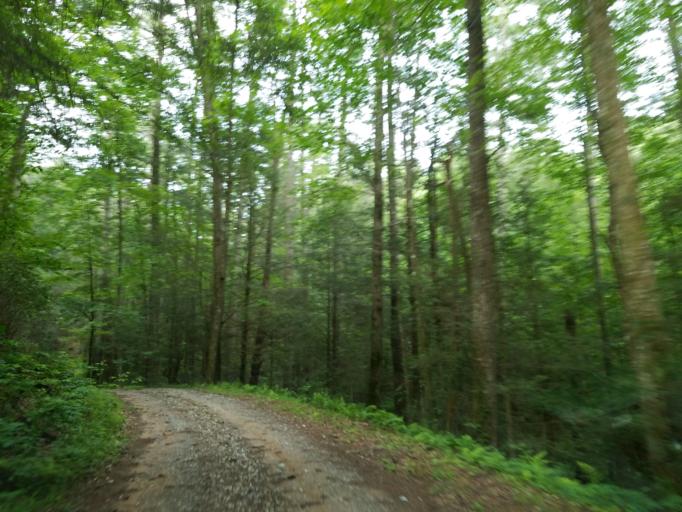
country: US
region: Georgia
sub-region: Union County
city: Blairsville
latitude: 34.7704
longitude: -84.0325
